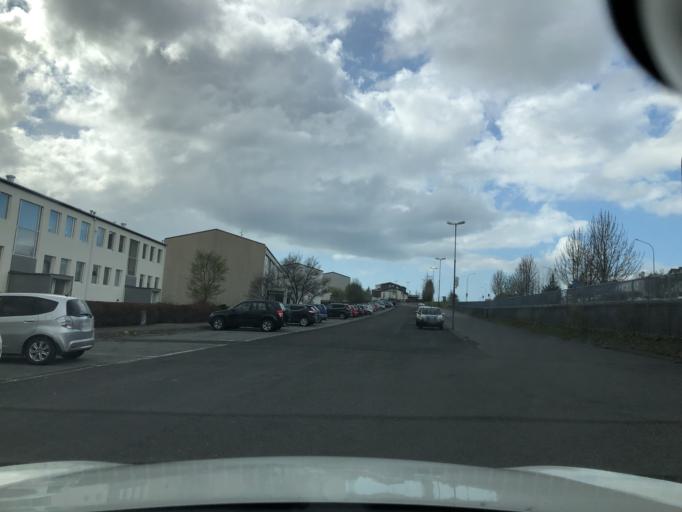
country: IS
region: Capital Region
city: Reykjavik
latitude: 64.1222
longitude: -21.8761
